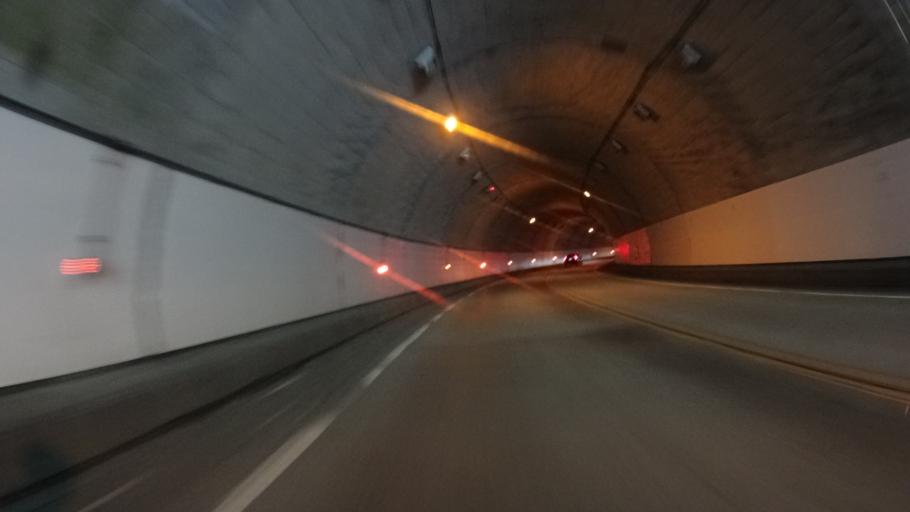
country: JP
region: Yamanashi
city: Enzan
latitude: 35.7538
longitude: 138.8103
